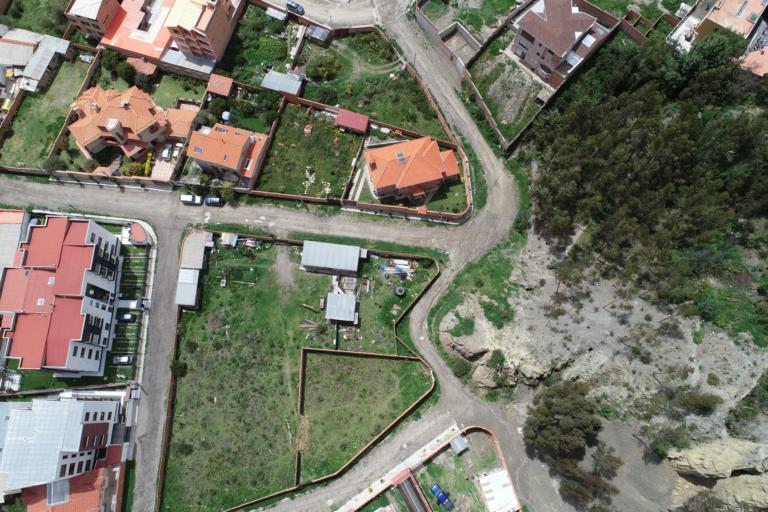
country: BO
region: La Paz
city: La Paz
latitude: -16.4989
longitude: -68.0820
